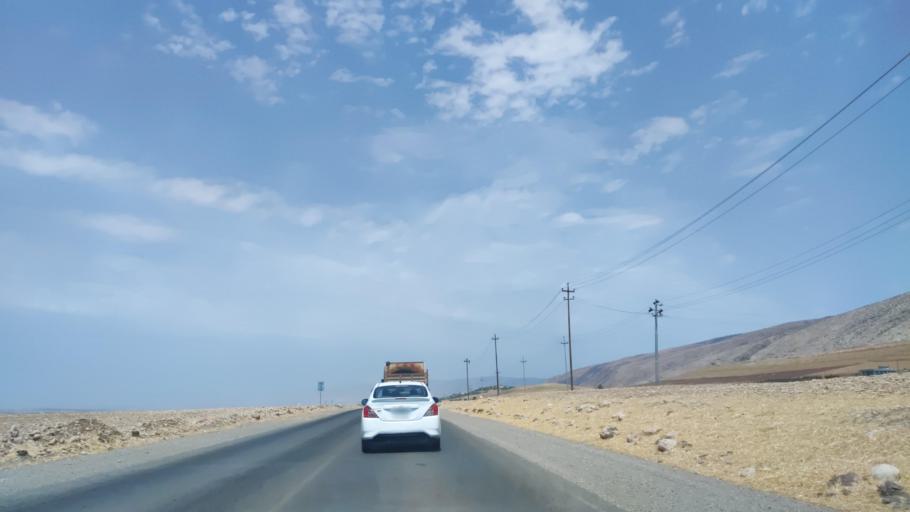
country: IQ
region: Arbil
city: Shaqlawah
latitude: 36.5179
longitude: 44.3703
